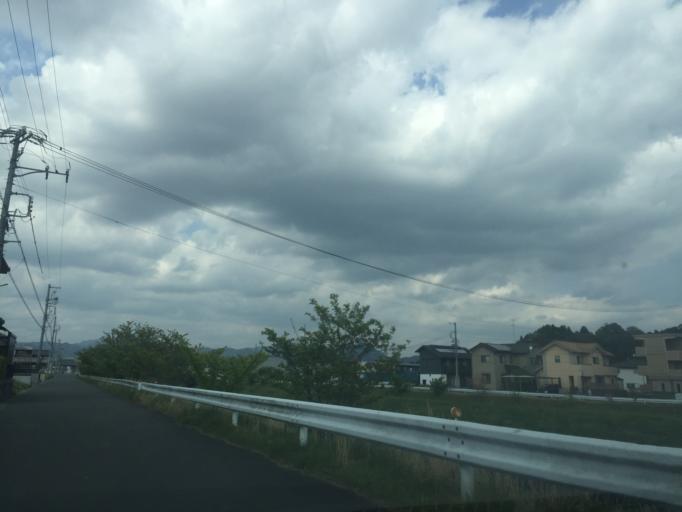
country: JP
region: Shizuoka
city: Kakegawa
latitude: 34.7837
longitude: 138.0104
